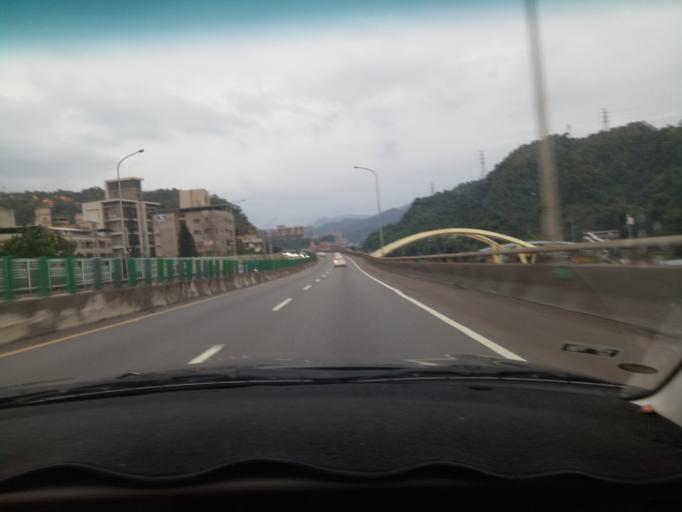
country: TW
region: Taiwan
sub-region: Keelung
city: Keelung
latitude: 25.1038
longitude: 121.7386
